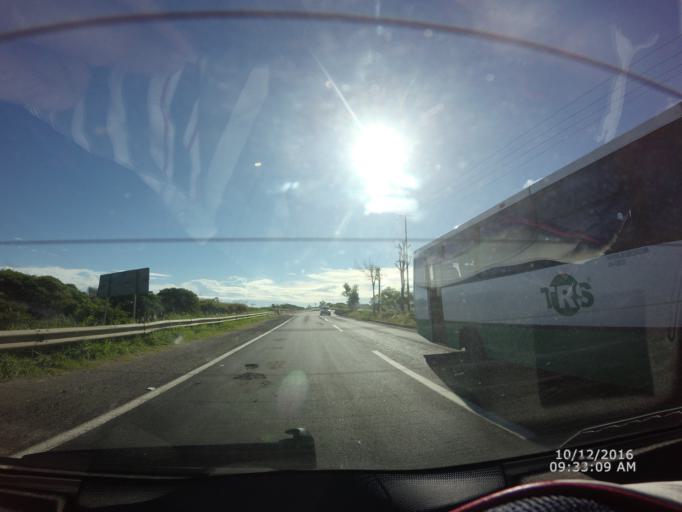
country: TR
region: Sivas
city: Karayun
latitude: 39.6691
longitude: 37.2981
